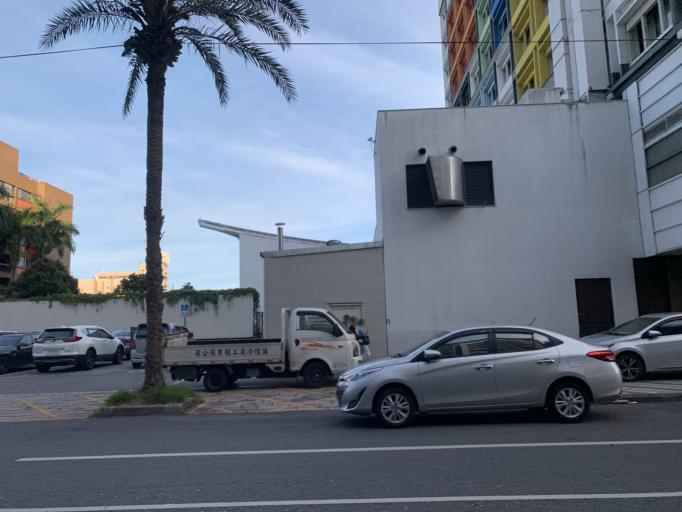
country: TW
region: Taiwan
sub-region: Hualien
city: Hualian
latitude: 23.9921
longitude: 121.6266
